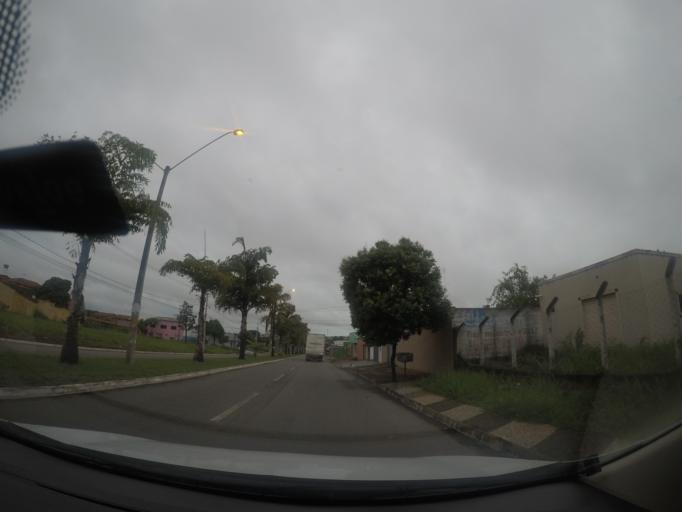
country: BR
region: Goias
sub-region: Goiania
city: Goiania
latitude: -16.7554
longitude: -49.3222
